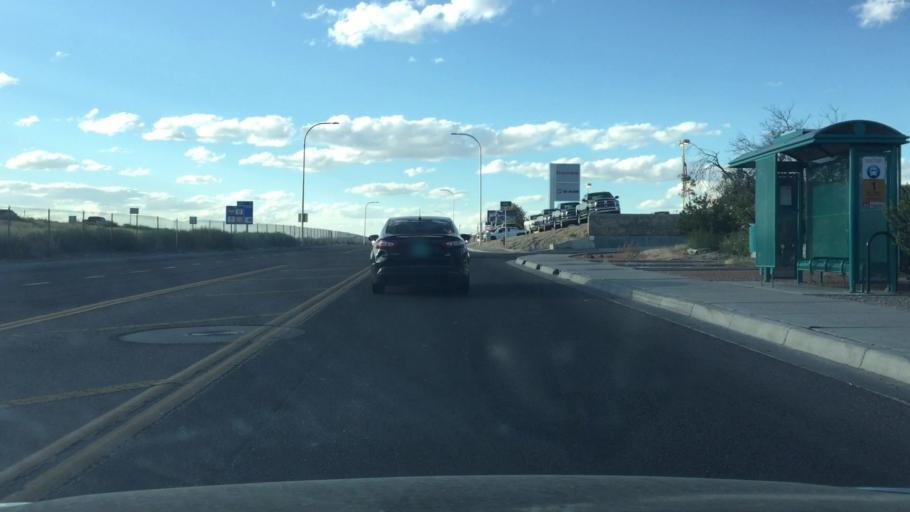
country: US
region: New Mexico
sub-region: Dona Ana County
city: Las Cruces
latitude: 32.3288
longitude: -106.7557
